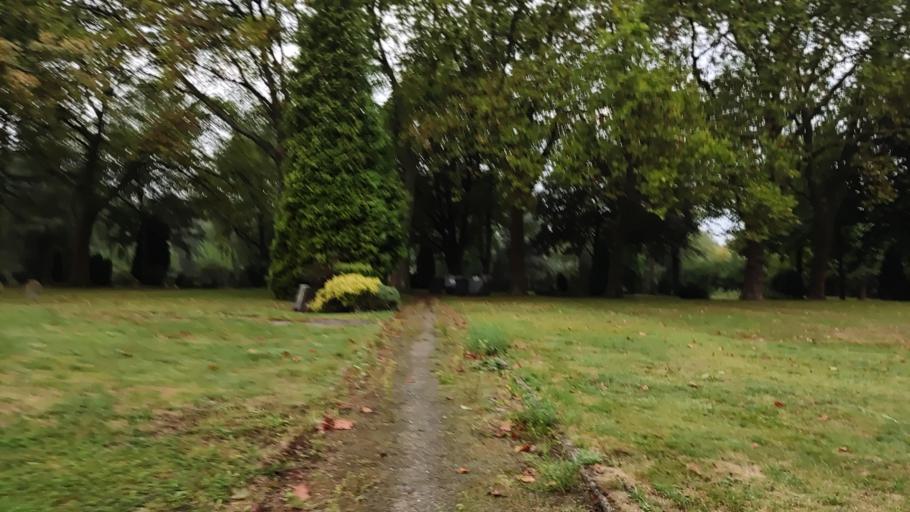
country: DE
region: North Rhine-Westphalia
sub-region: Regierungsbezirk Arnsberg
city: Herne
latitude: 51.5485
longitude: 7.2376
